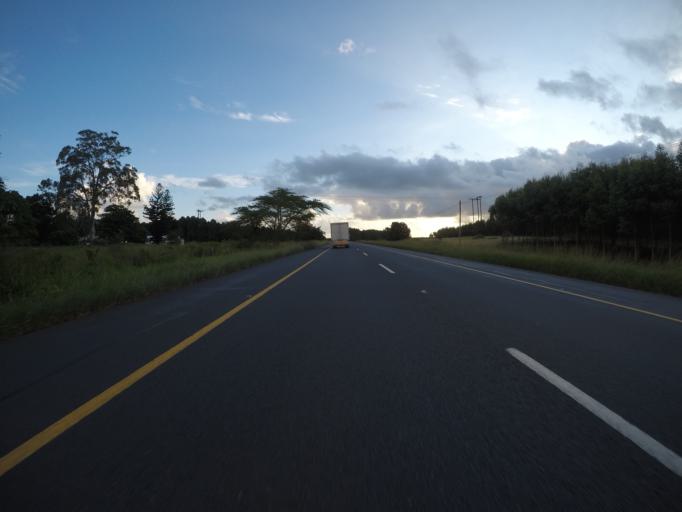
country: ZA
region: KwaZulu-Natal
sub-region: uThungulu District Municipality
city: KwaMbonambi
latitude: -28.5744
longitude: 32.1072
